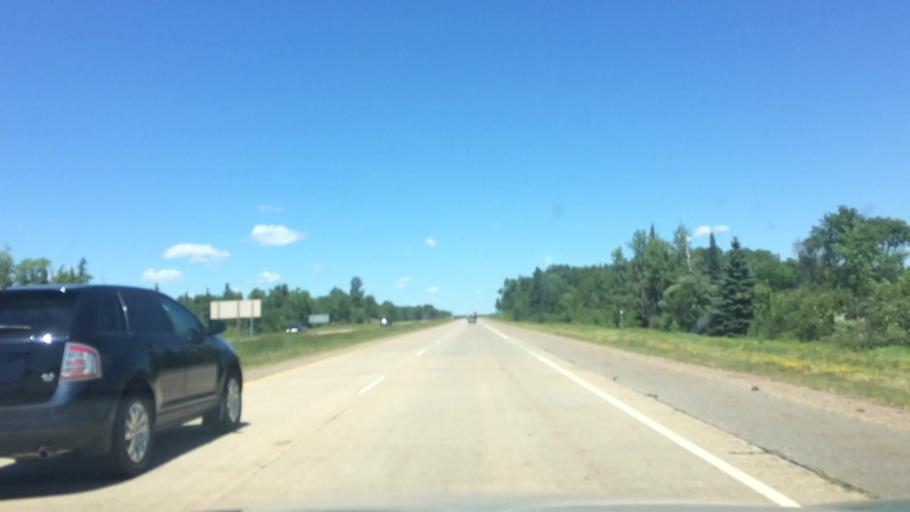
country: US
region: Wisconsin
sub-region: Lincoln County
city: Tomahawk
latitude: 45.3945
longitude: -89.6721
